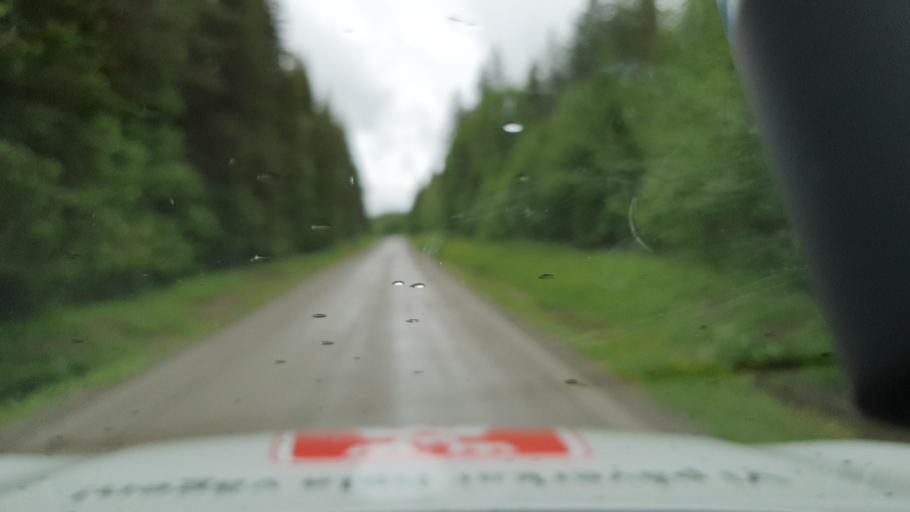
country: SE
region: Vaesterbotten
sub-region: Dorotea Kommun
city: Dorotea
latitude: 64.0504
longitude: 16.7299
